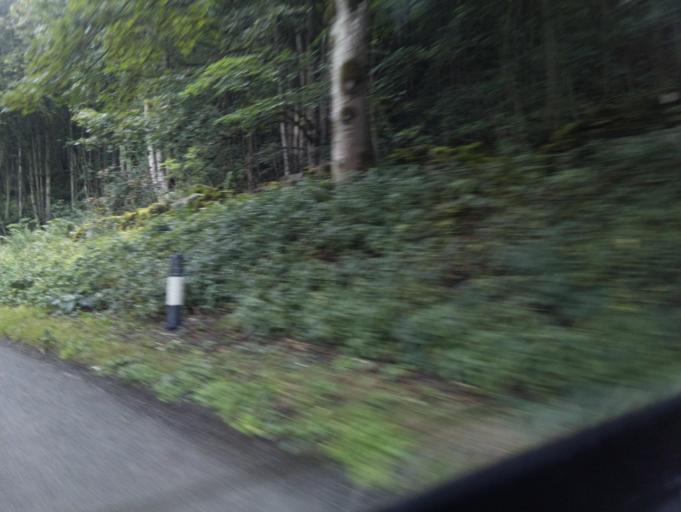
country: GB
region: England
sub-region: North Yorkshire
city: Leyburn
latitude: 54.3870
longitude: -1.8267
